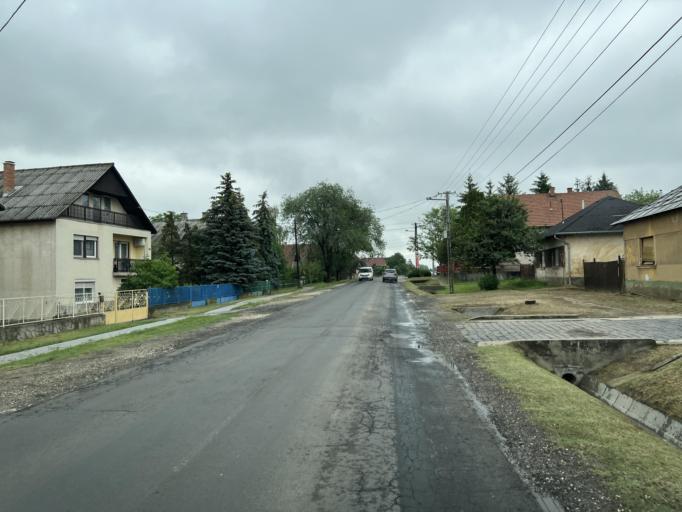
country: HU
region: Pest
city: Galgaheviz
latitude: 47.6185
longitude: 19.5711
